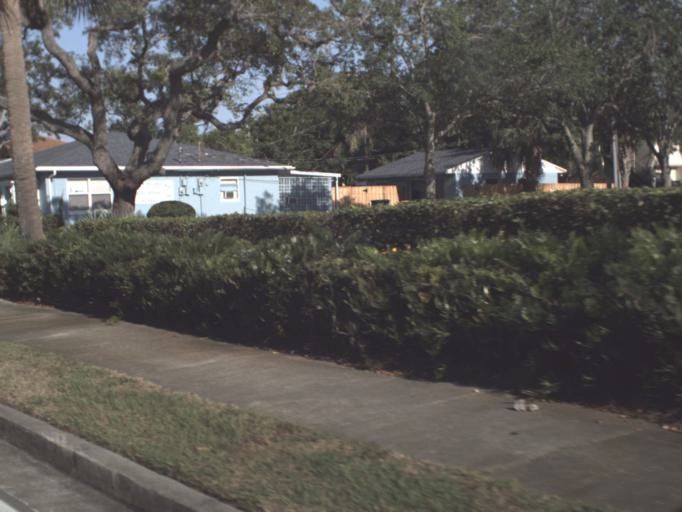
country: US
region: Florida
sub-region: Brevard County
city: Melbourne
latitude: 28.0794
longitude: -80.6126
